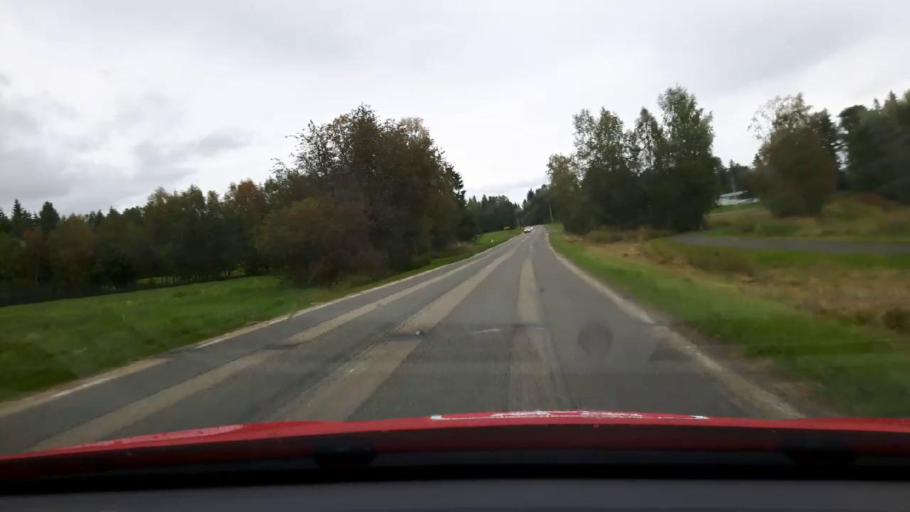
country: SE
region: Jaemtland
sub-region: Bergs Kommun
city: Hoverberg
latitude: 62.7800
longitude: 14.4319
